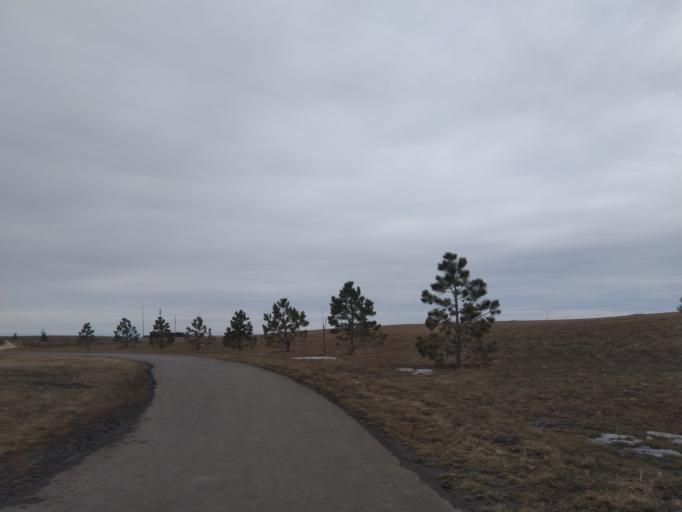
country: CA
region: Alberta
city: Chestermere
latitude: 51.1115
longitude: -113.9248
